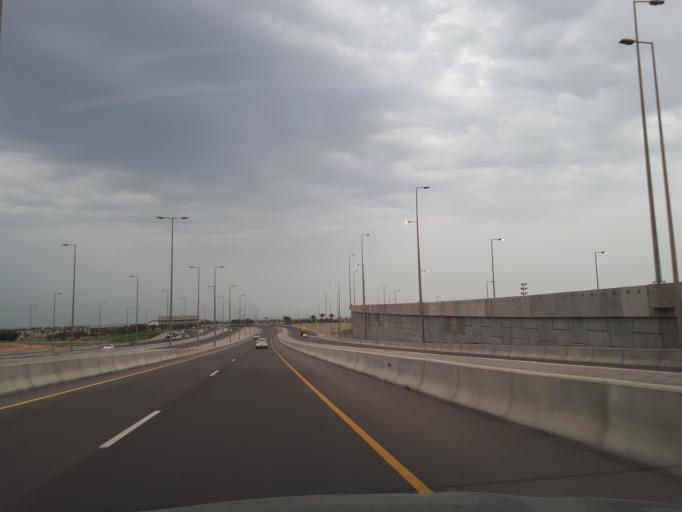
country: OM
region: Muhafazat Masqat
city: Bawshar
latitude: 23.5861
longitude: 58.3327
